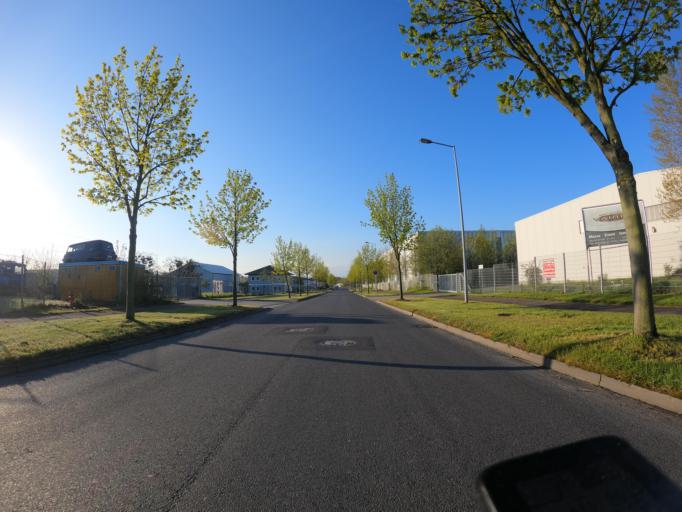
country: DE
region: Brandenburg
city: Neuenhagen
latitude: 52.5349
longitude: 13.7108
